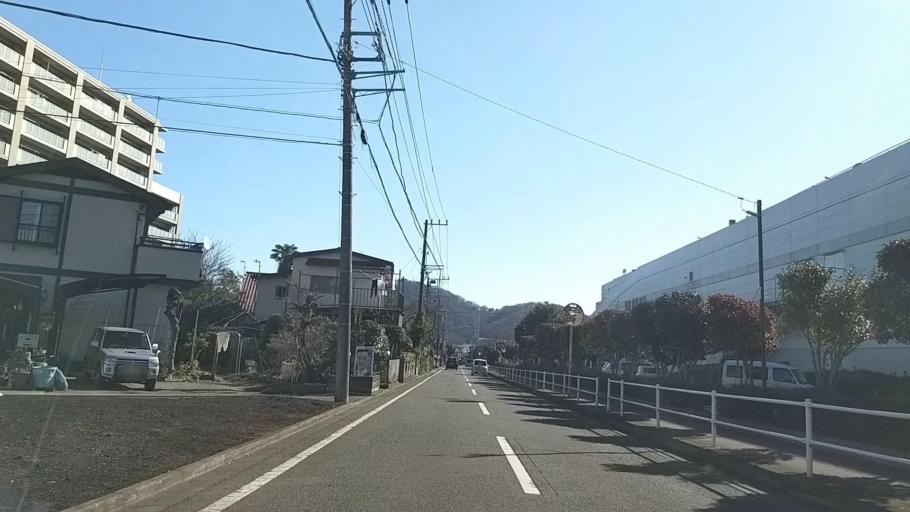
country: JP
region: Kanagawa
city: Hadano
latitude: 35.3791
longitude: 139.2282
